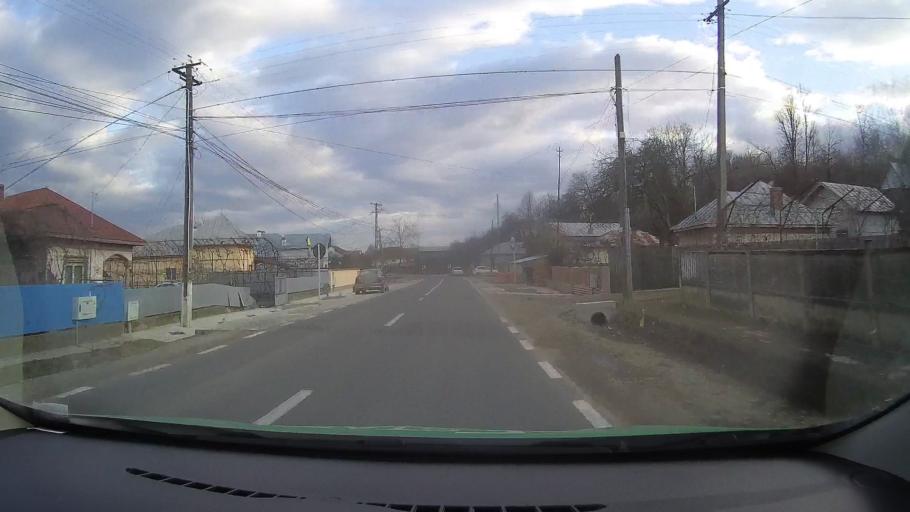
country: RO
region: Dambovita
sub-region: Comuna I. L. Caragiale
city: Mija
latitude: 44.9179
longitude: 25.6890
